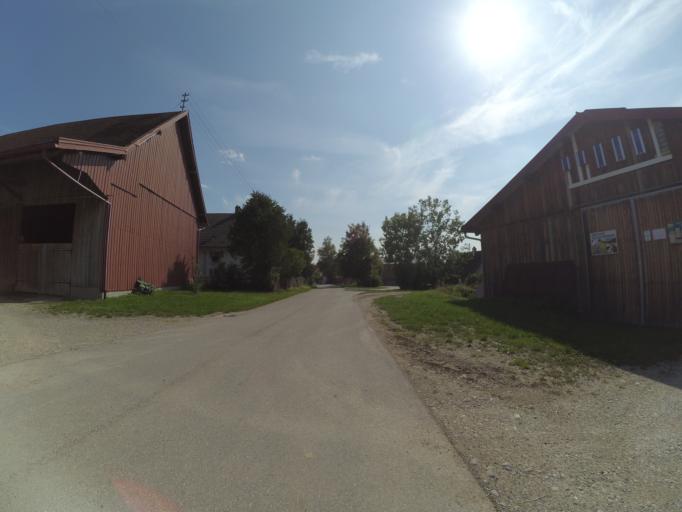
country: DE
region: Bavaria
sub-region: Swabia
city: Lamerdingen
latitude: 48.0865
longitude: 10.7684
